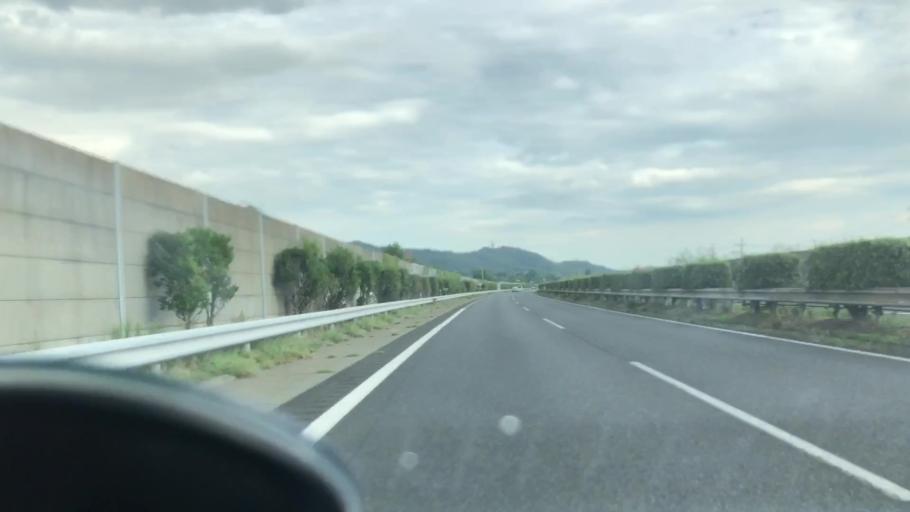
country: JP
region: Hyogo
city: Ono
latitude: 34.9383
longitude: 134.8303
